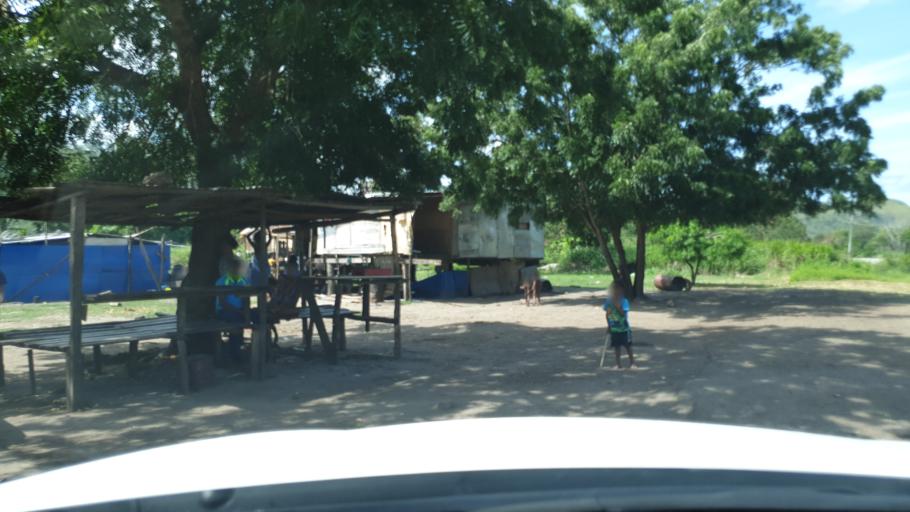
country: PG
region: Central Province
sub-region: Rigo
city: Kwikila
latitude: -9.8920
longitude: 147.5816
